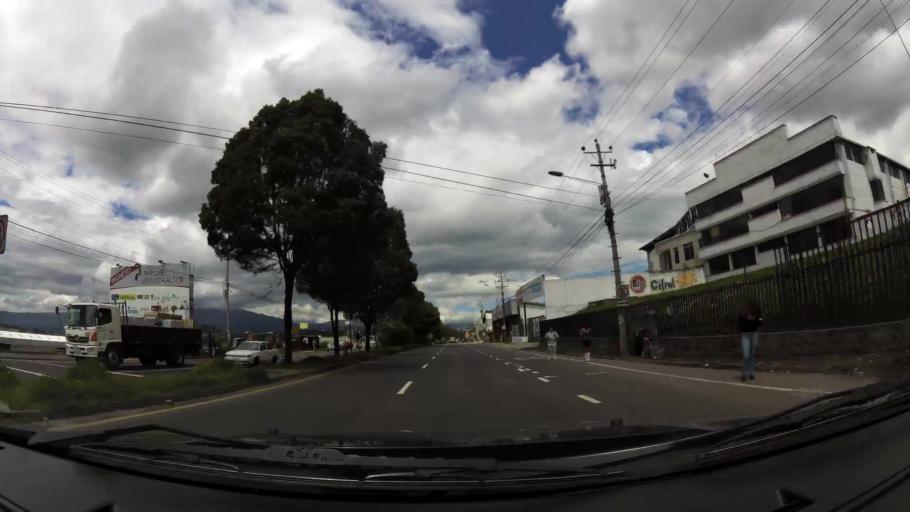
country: EC
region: Pichincha
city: Sangolqui
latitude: -0.3452
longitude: -78.5487
